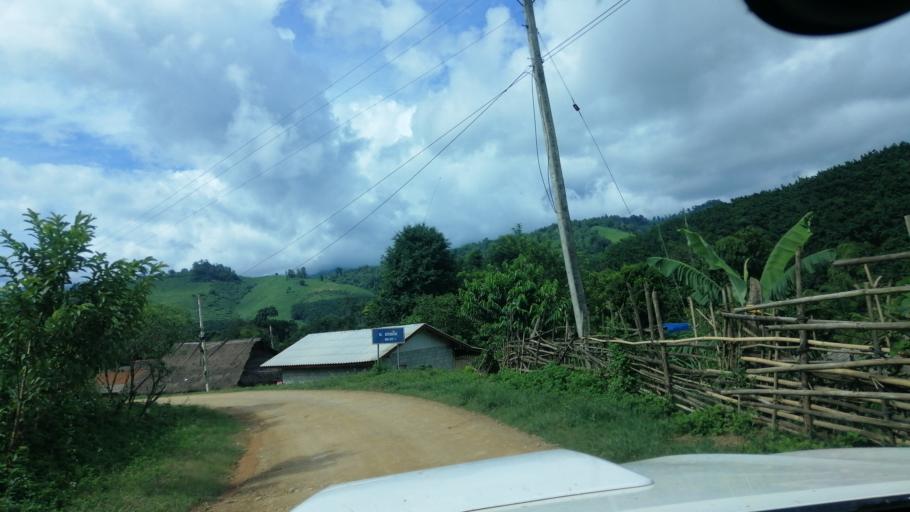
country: TH
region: Phayao
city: Phu Sang
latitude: 19.6215
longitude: 100.5386
